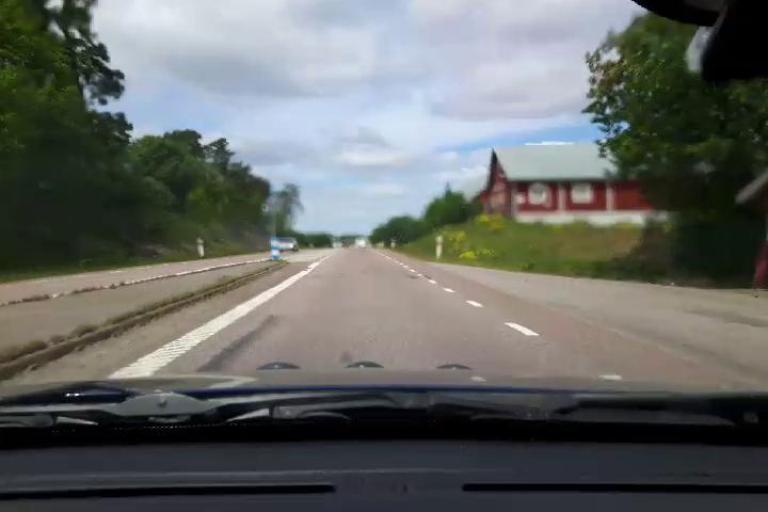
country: SE
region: Uppsala
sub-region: Uppsala Kommun
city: Gamla Uppsala
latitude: 59.9060
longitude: 17.6097
